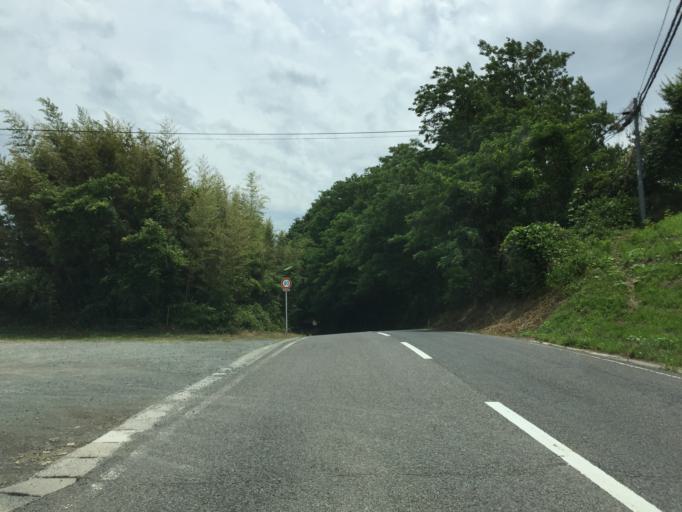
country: JP
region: Fukushima
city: Miharu
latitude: 37.4283
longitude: 140.4991
